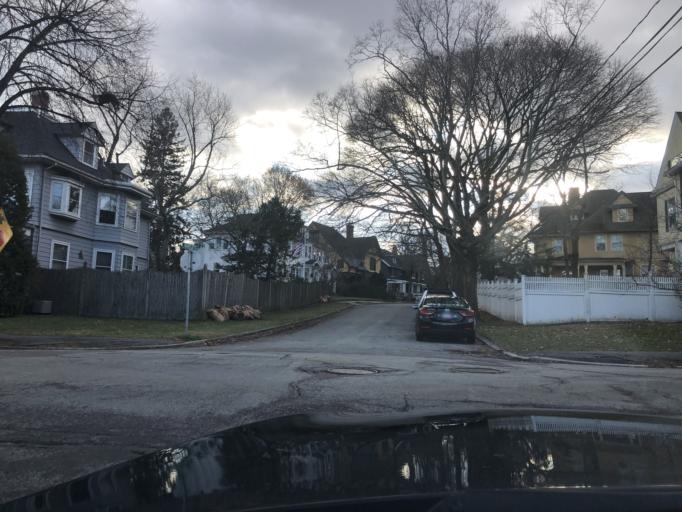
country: US
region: Massachusetts
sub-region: Middlesex County
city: Arlington
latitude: 42.4125
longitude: -71.1625
